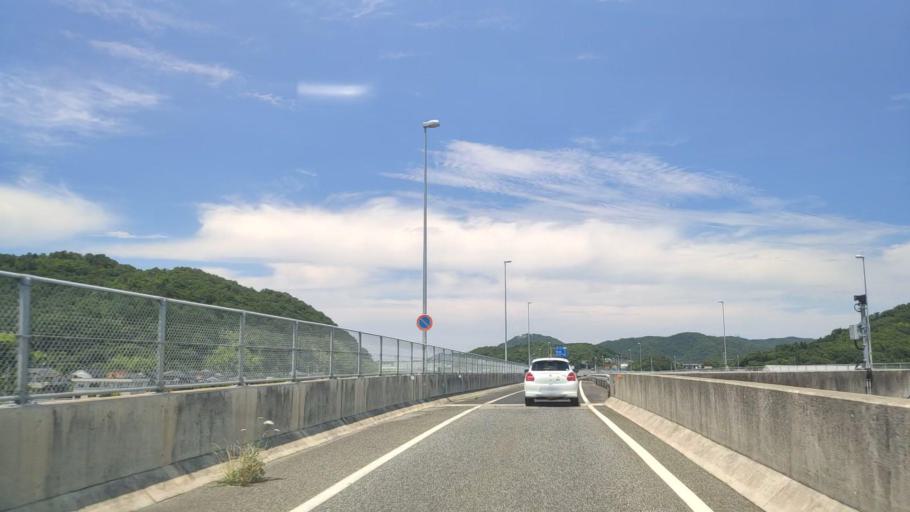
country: JP
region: Tottori
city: Tottori
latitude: 35.4648
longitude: 134.2429
